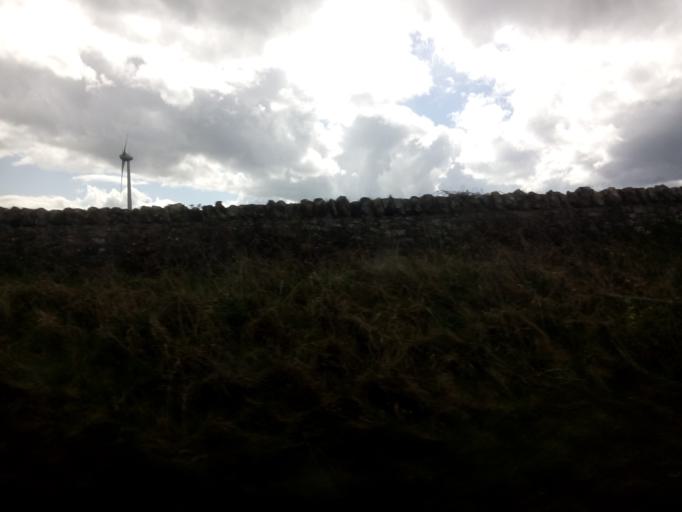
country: GB
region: England
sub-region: Northumberland
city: Berwick-Upon-Tweed
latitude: 55.7964
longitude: -2.0198
